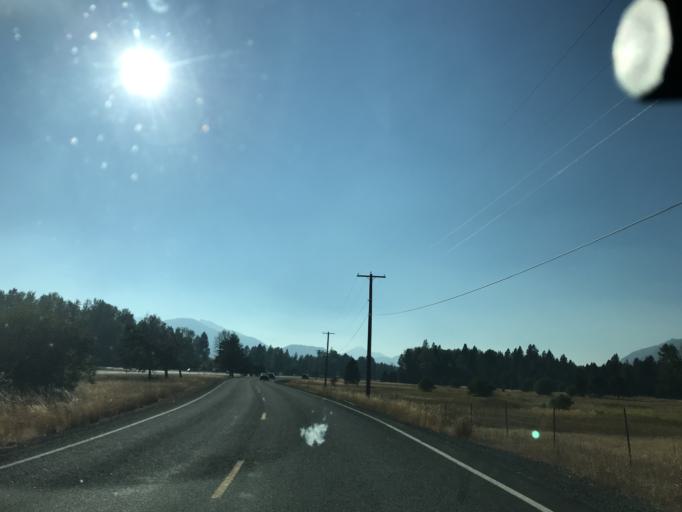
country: US
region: Washington
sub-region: Kittitas County
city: Cle Elum
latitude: 47.1961
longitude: -121.0532
